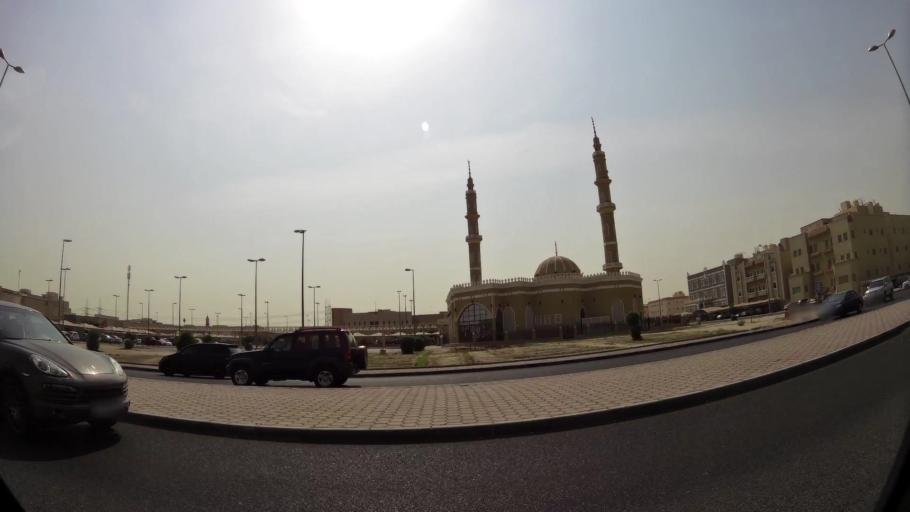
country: KW
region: Al Asimah
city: Ar Rabiyah
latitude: 29.3025
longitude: 47.8992
